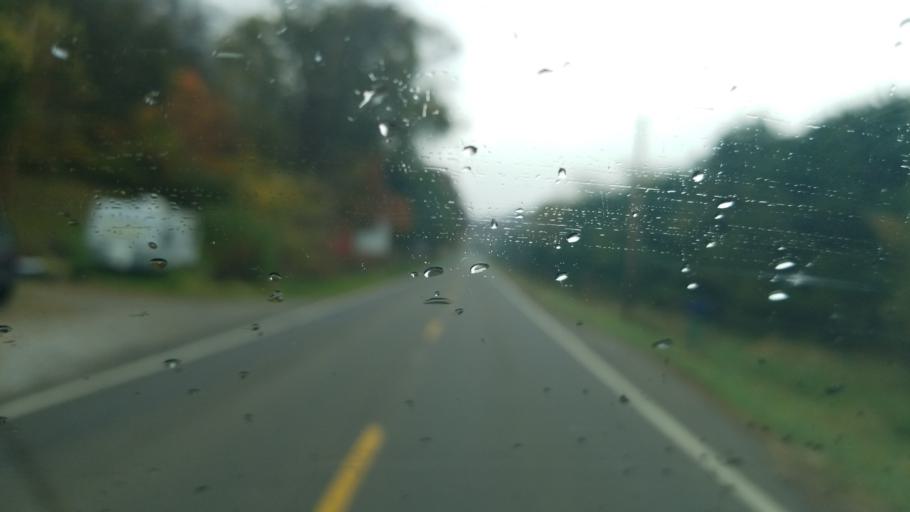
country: US
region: Ohio
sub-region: Holmes County
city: Millersburg
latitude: 40.5121
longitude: -81.9202
